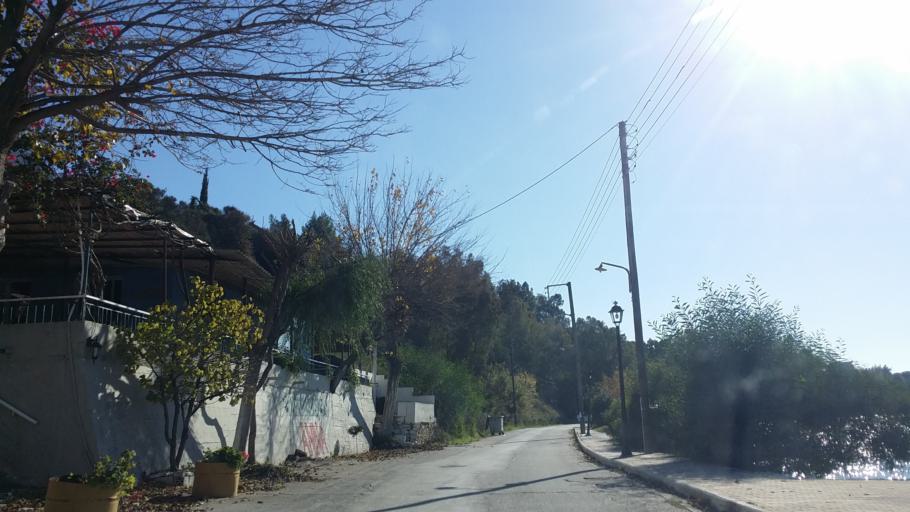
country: GR
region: West Greece
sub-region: Nomos Aitolias kai Akarnanias
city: Palairos
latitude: 38.7782
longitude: 20.8810
